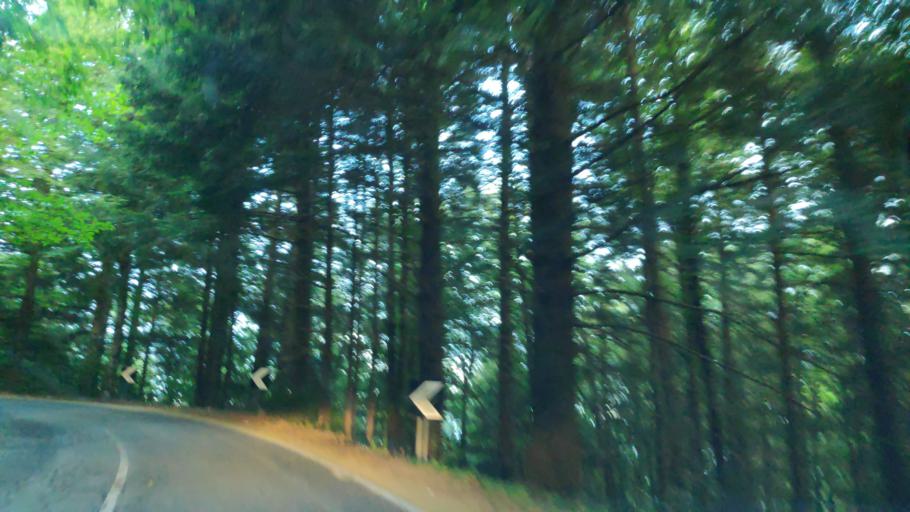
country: IT
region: Calabria
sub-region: Provincia di Vibo-Valentia
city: Mongiana
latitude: 38.5299
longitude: 16.3309
